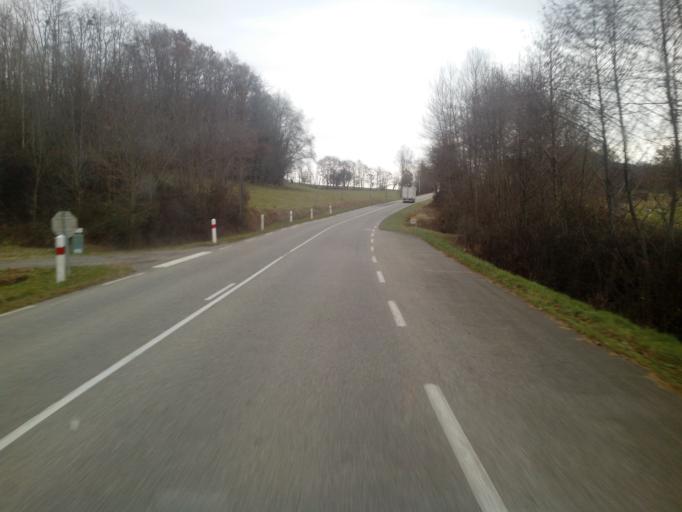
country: FR
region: Midi-Pyrenees
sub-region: Departement de l'Ariege
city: Montjoie-en-Couserans
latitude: 42.9962
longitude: 1.3048
